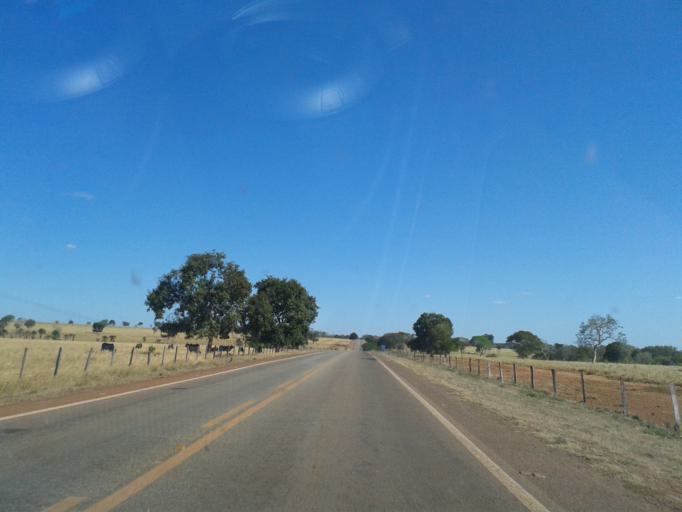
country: BR
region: Goias
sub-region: Crixas
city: Crixas
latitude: -14.1503
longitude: -50.3607
